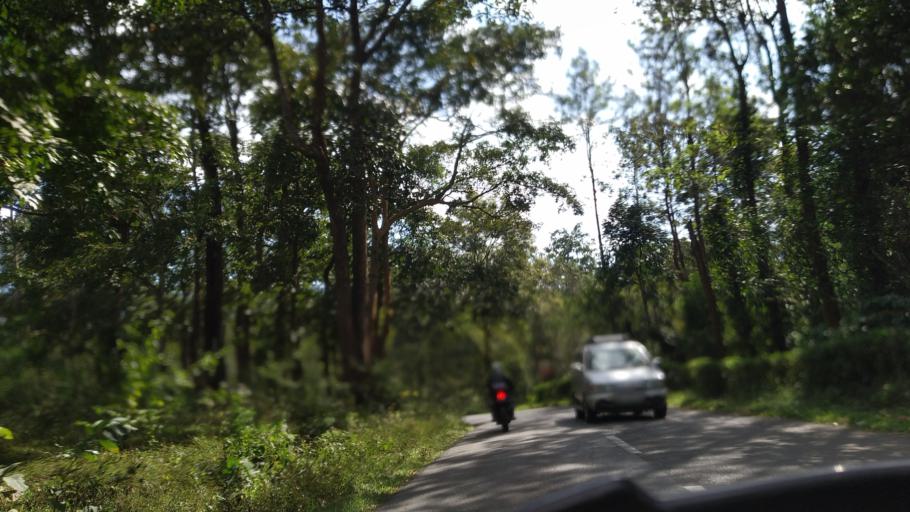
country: IN
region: Kerala
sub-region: Wayanad
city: Panamaram
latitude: 11.9345
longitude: 76.0642
